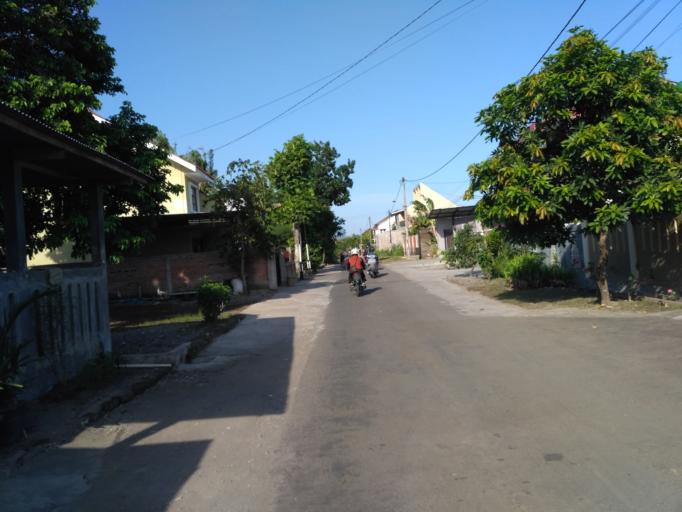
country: ID
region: Daerah Istimewa Yogyakarta
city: Depok
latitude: -7.7737
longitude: 110.4246
